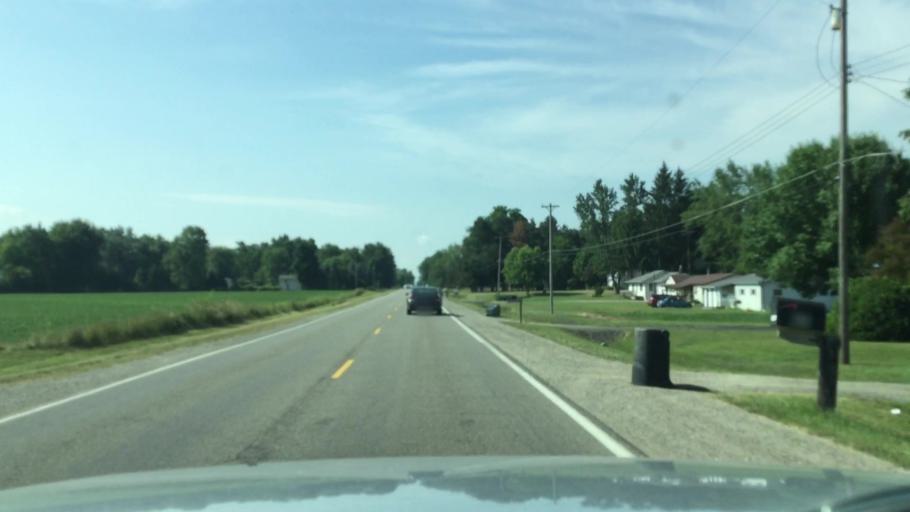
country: US
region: Michigan
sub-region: Genesee County
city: Flushing
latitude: 43.1103
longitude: -83.8137
